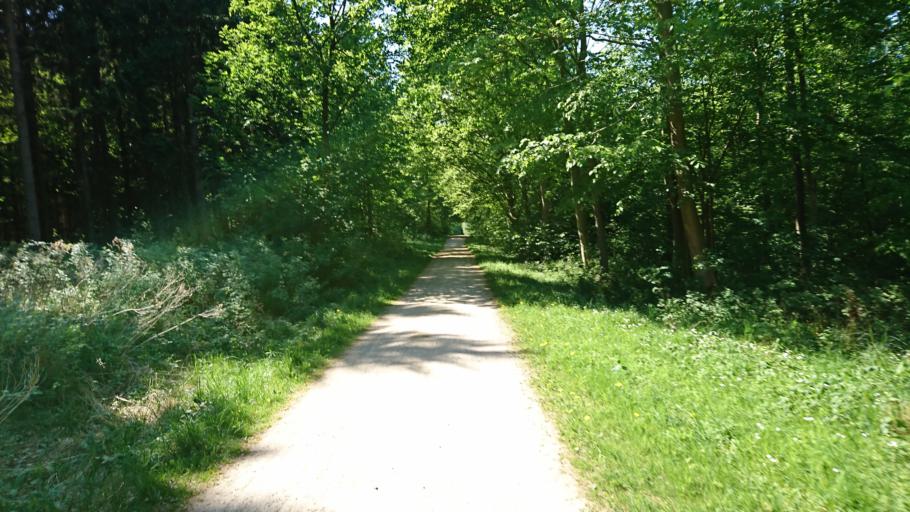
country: DK
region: Capital Region
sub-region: Ballerup Kommune
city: Ballerup
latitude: 55.7570
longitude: 12.3535
